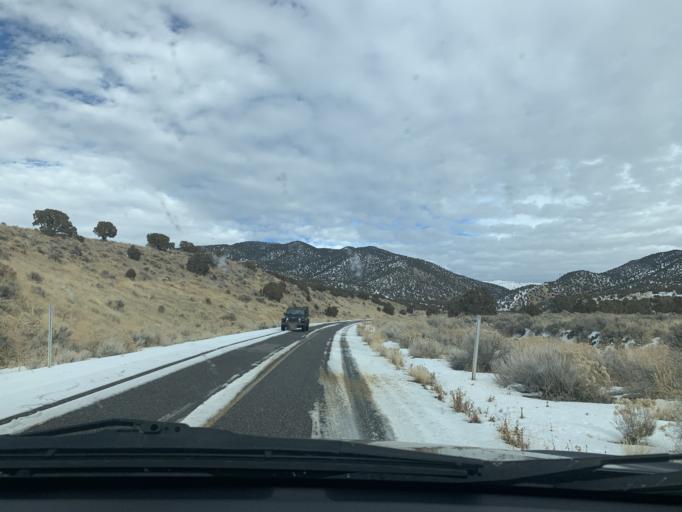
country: US
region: Utah
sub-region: Tooele County
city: Tooele
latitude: 40.3030
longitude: -112.2653
